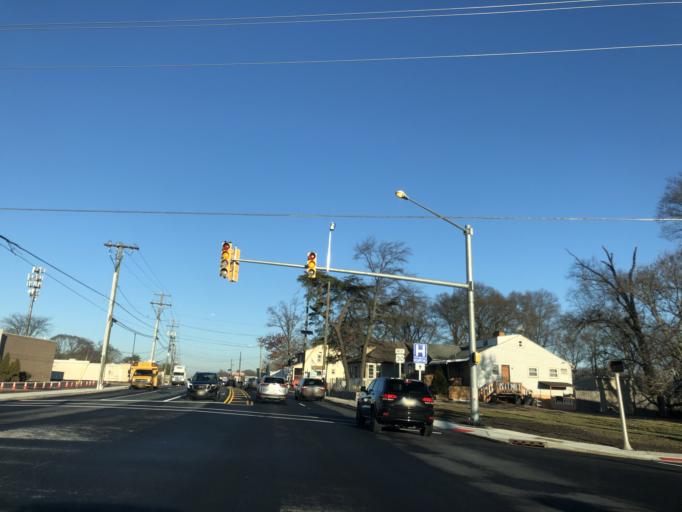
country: US
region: New Jersey
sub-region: Camden County
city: Lawnside
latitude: 39.8561
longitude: -75.0277
